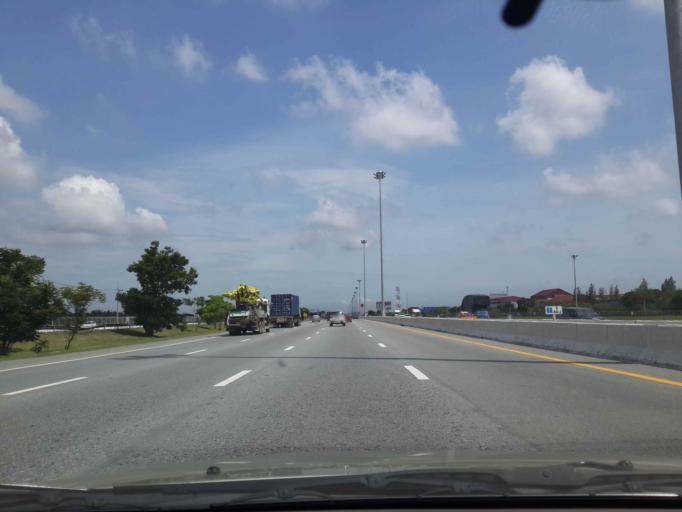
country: TH
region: Chachoengsao
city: Bang Pakong
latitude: 13.5998
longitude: 100.9530
